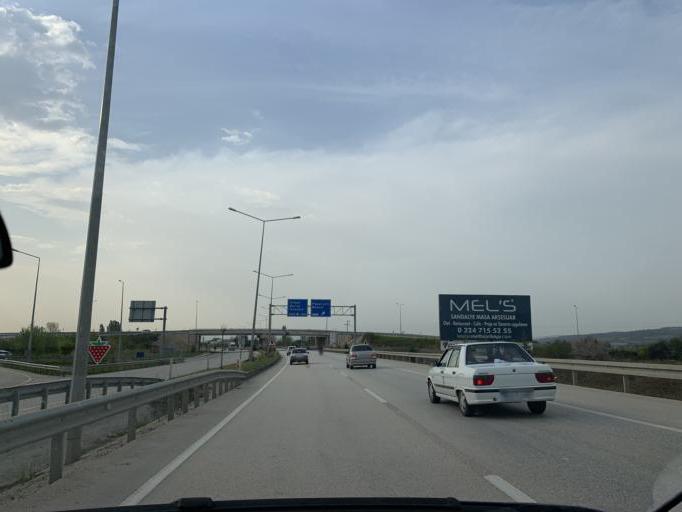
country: TR
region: Bursa
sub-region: Inegoel
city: Inegol
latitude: 40.0570
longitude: 29.5861
